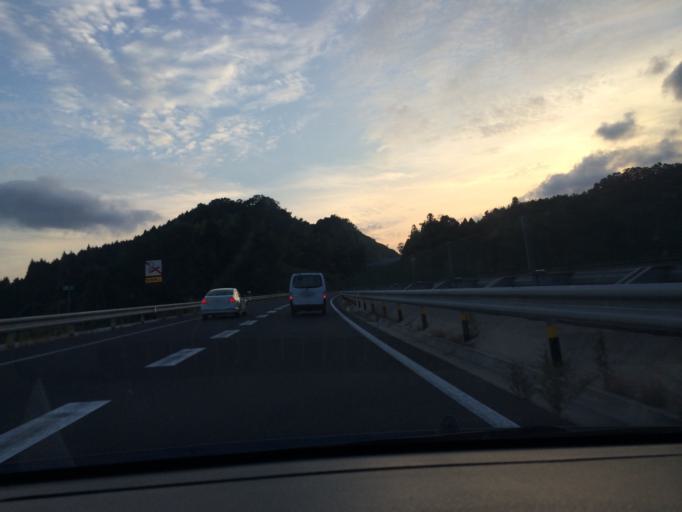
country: JP
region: Shimane
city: Izumo
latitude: 35.3395
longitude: 132.8124
